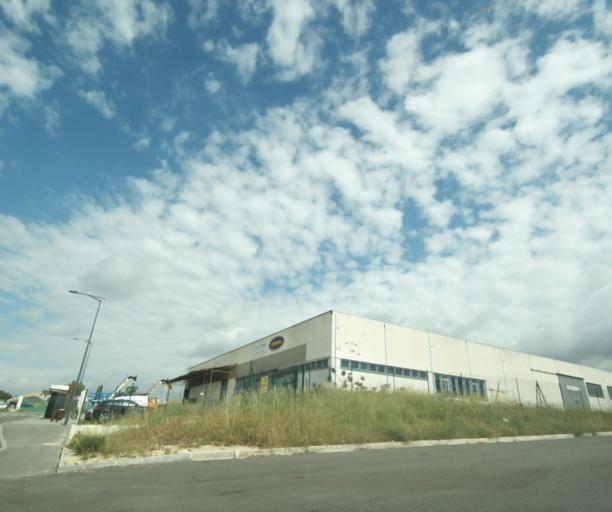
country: FR
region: Provence-Alpes-Cote d'Azur
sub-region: Departement des Bouches-du-Rhone
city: Vitrolles
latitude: 43.4403
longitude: 5.2413
